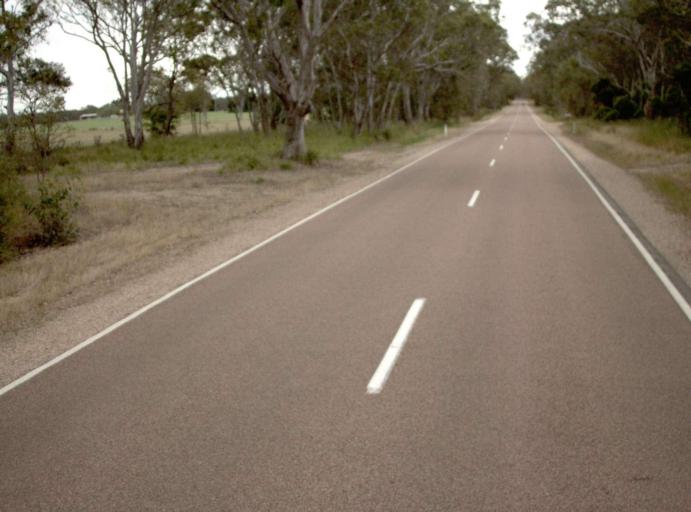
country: AU
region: Victoria
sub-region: Wellington
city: Sale
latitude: -38.0010
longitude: 147.3225
